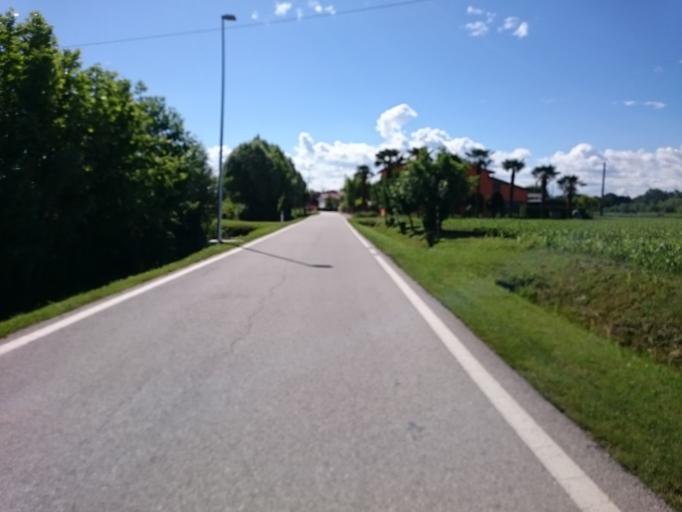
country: IT
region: Veneto
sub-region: Provincia di Padova
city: Saonara
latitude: 45.3582
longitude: 11.9999
